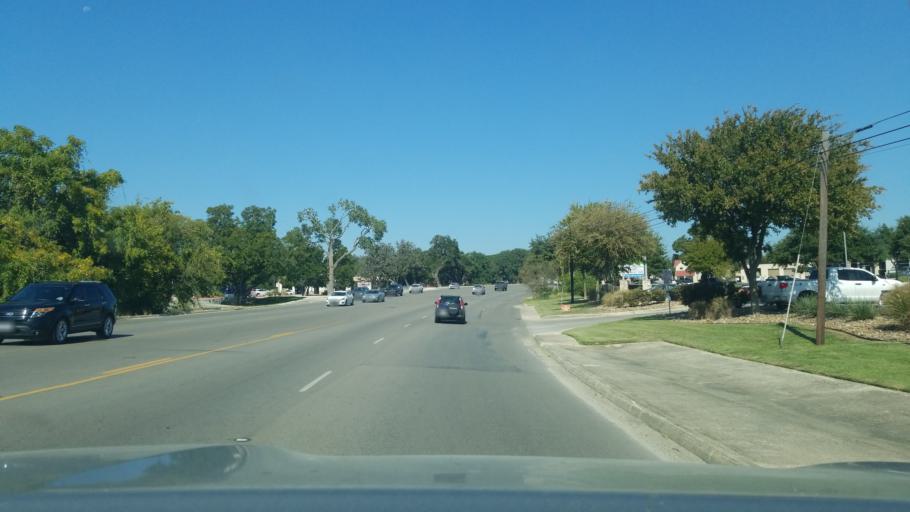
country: US
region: Texas
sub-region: Kendall County
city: Boerne
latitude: 29.7775
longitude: -98.7269
